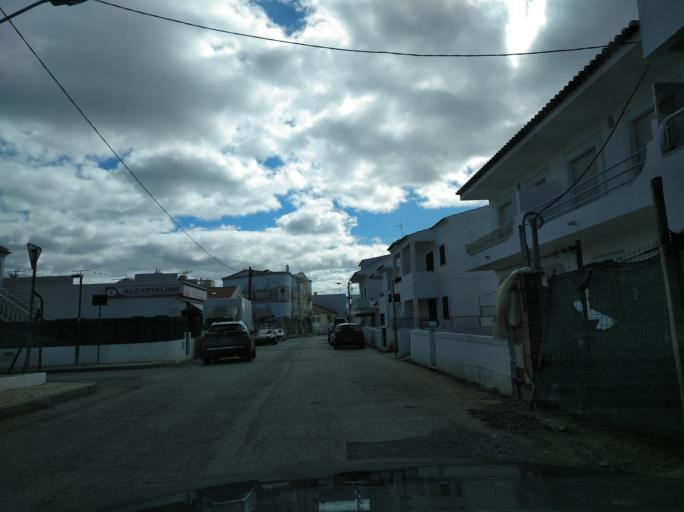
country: PT
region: Faro
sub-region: Vila Real de Santo Antonio
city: Monte Gordo
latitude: 37.1759
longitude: -7.4997
